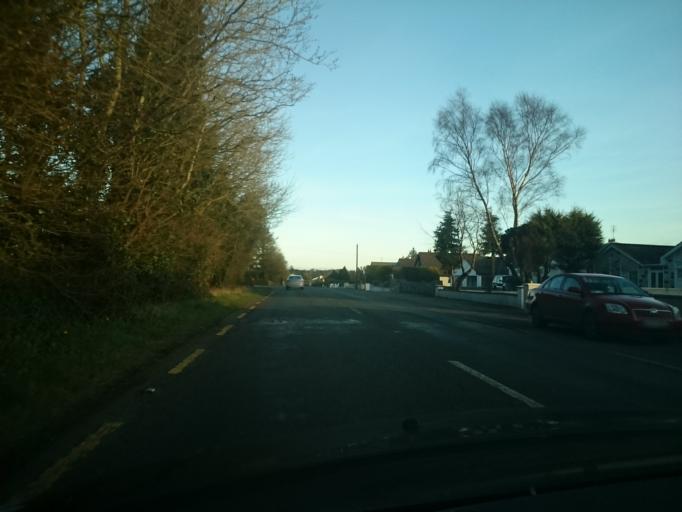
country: IE
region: Connaught
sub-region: Maigh Eo
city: Claremorris
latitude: 53.7431
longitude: -9.0166
